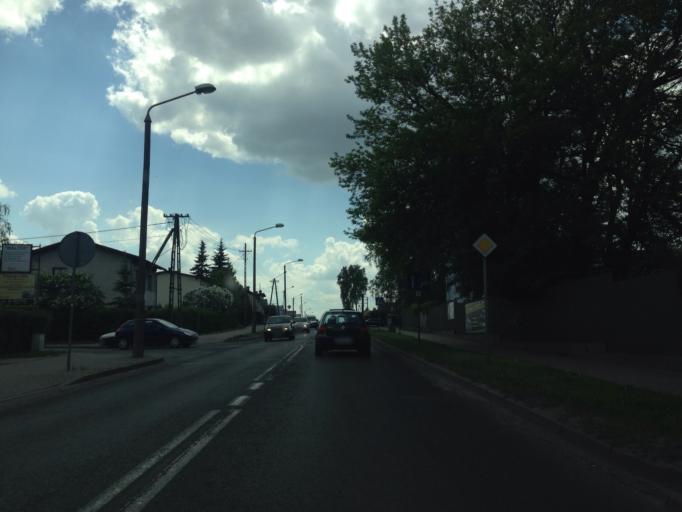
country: PL
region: Kujawsko-Pomorskie
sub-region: Powiat brodnicki
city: Brodnica
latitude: 53.2455
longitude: 19.3972
